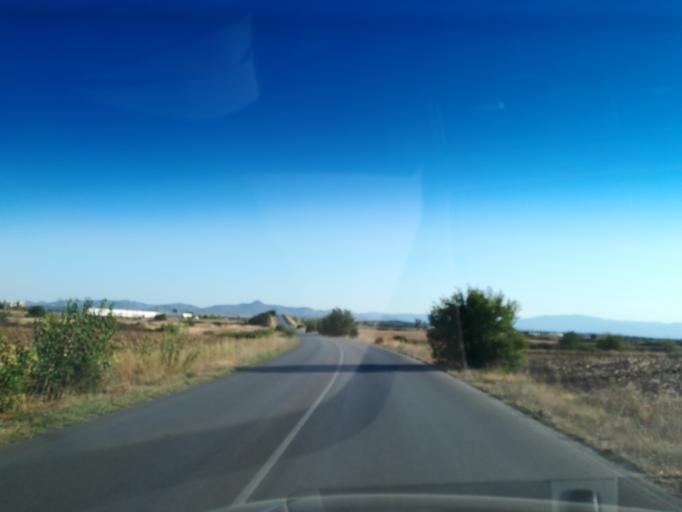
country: BG
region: Stara Zagora
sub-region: Obshtina Chirpan
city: Chirpan
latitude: 42.1031
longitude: 25.2101
